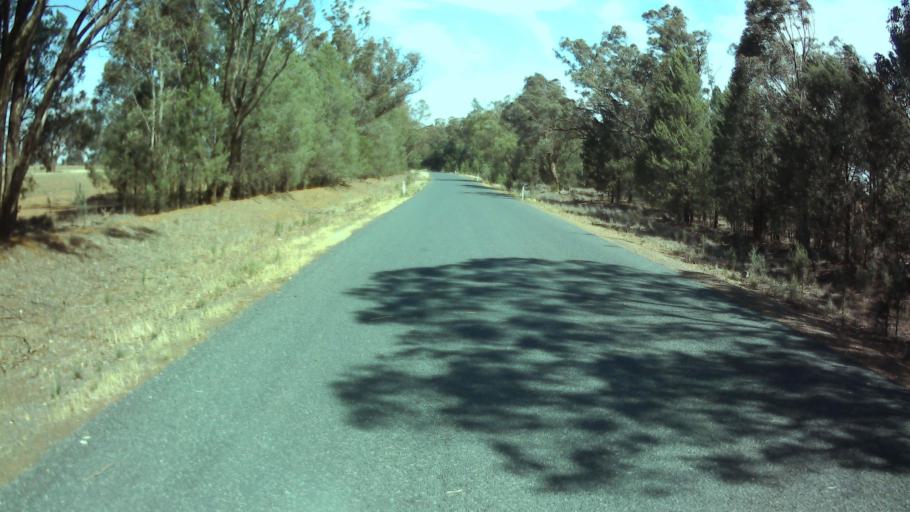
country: AU
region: New South Wales
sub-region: Weddin
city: Grenfell
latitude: -34.0563
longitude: 148.1302
